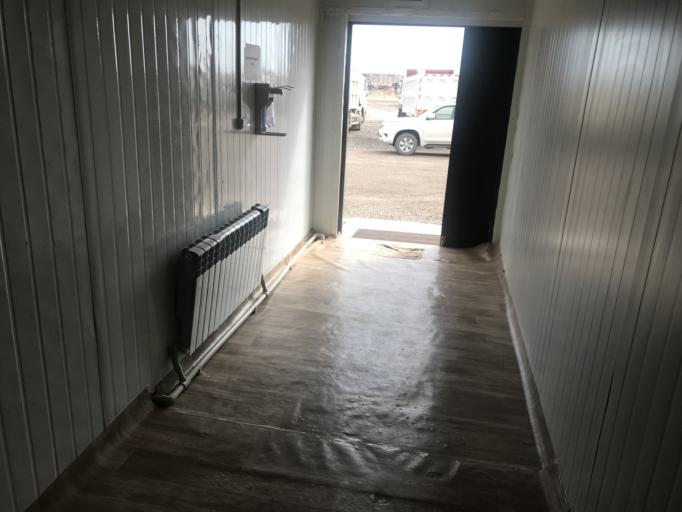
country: KZ
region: Almaty Oblysy
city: Ulken
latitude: 45.1617
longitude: 73.9387
